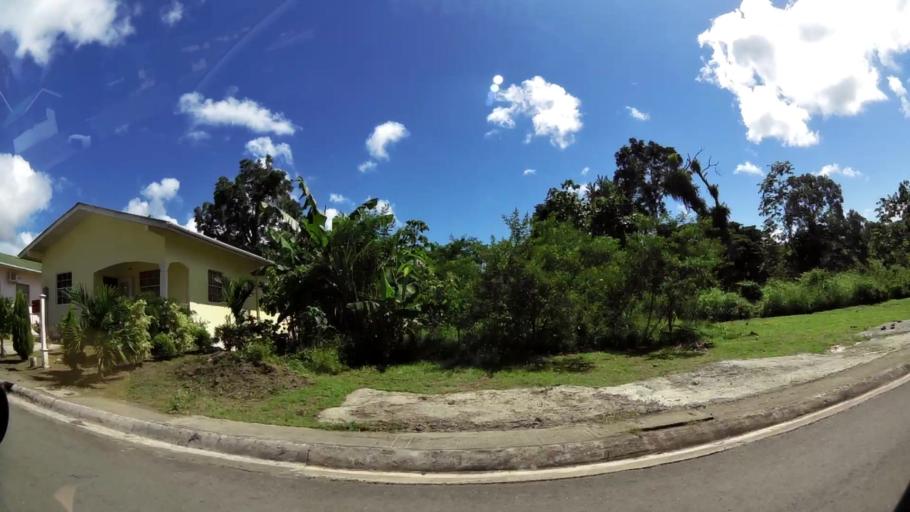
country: TT
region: Tobago
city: Scarborough
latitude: 11.2180
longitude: -60.7714
